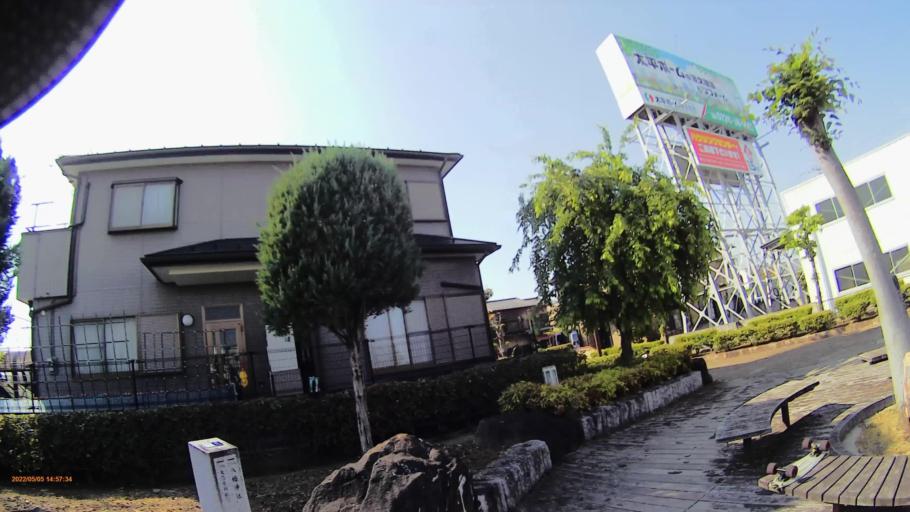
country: JP
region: Saitama
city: Sugito
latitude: 36.0210
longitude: 139.7439
